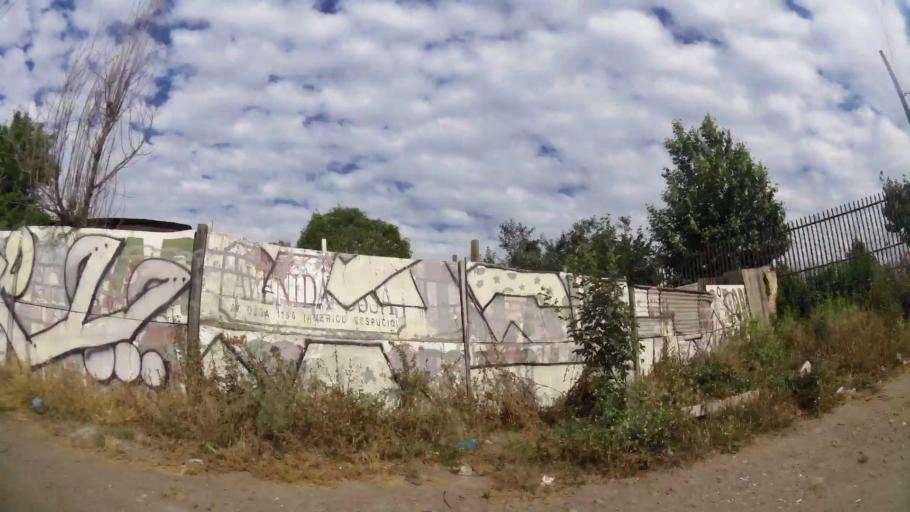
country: CL
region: Santiago Metropolitan
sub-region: Provincia de Santiago
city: La Pintana
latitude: -33.6205
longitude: -70.6191
